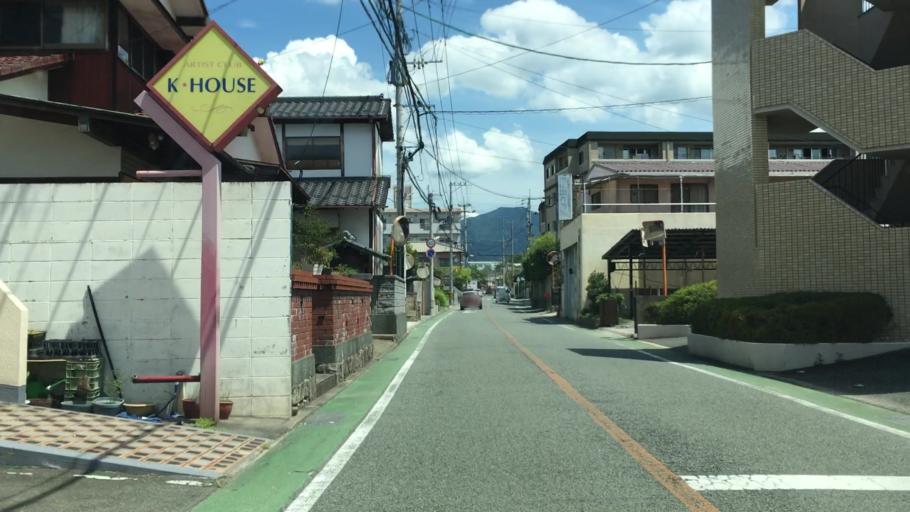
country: JP
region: Fukuoka
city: Dazaifu
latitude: 33.5159
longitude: 130.5271
